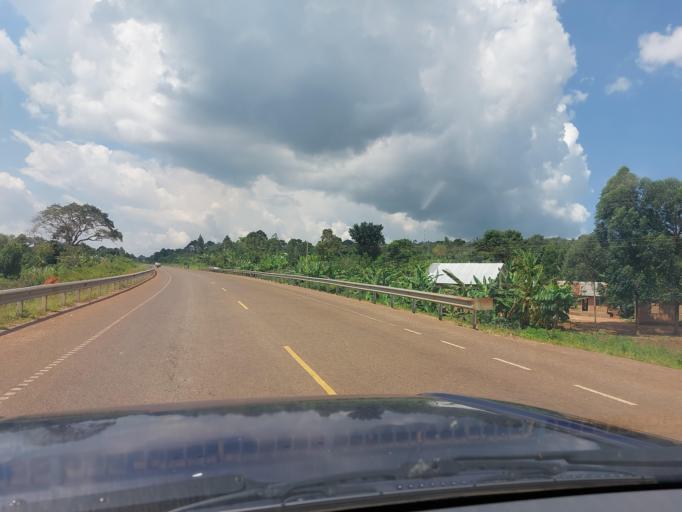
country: UG
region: Central Region
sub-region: Buikwe District
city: Buikwe
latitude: 0.3219
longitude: 33.1133
